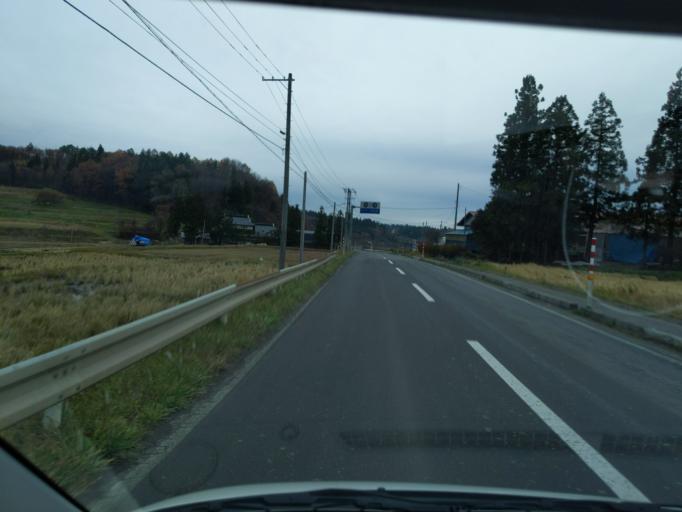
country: JP
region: Iwate
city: Kitakami
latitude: 39.2705
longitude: 141.2677
